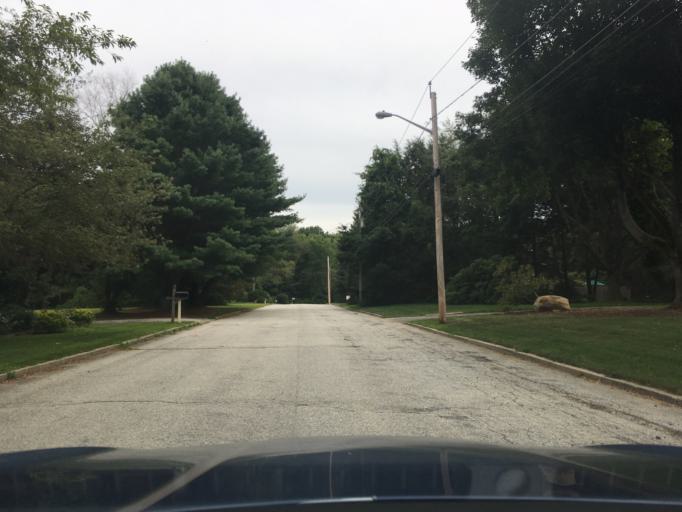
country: US
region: Rhode Island
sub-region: Kent County
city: East Greenwich
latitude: 41.6249
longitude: -71.5000
